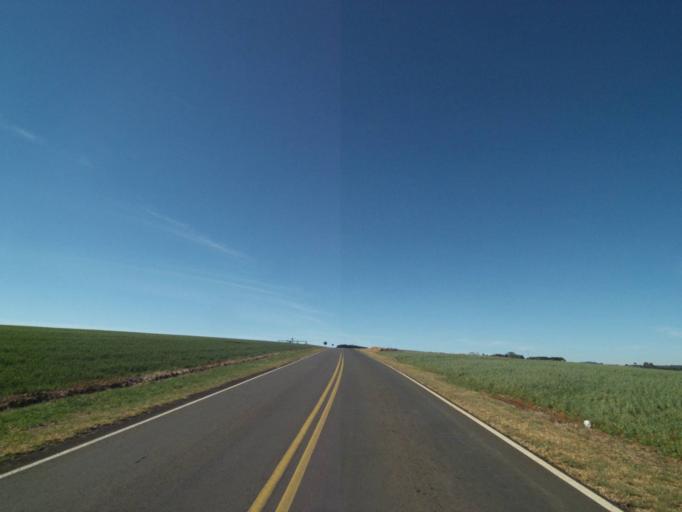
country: BR
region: Parana
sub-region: Tibagi
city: Tibagi
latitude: -24.5368
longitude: -50.3132
